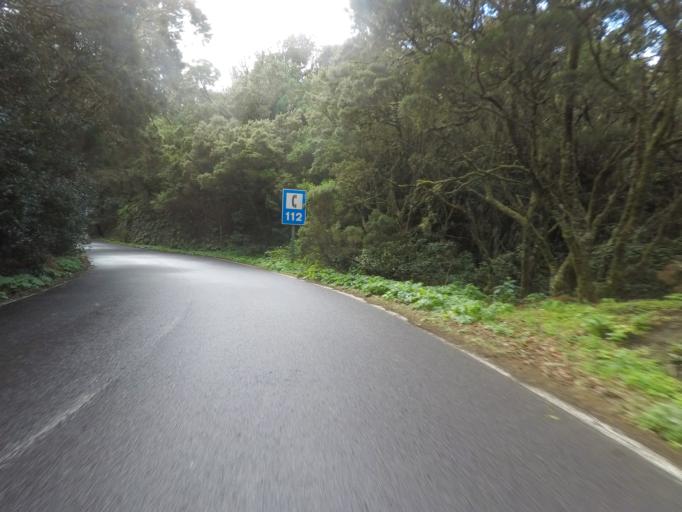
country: ES
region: Canary Islands
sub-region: Provincia de Santa Cruz de Tenerife
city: Vallehermosa
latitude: 28.1618
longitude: -17.2986
